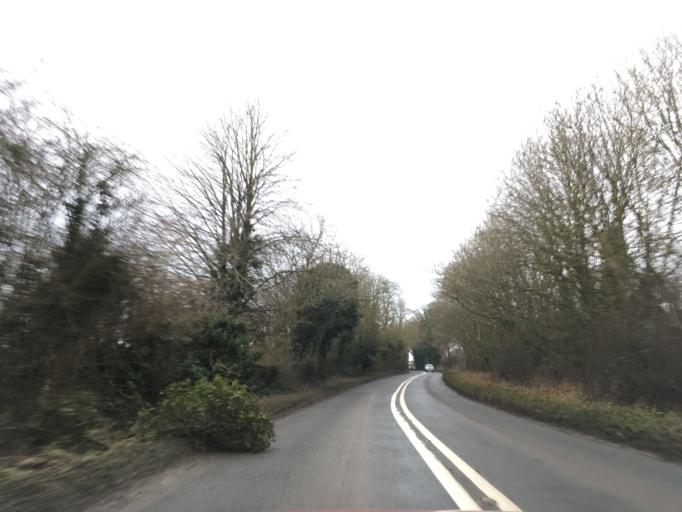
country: GB
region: England
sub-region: Gloucestershire
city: Tetbury
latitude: 51.6401
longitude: -2.1806
